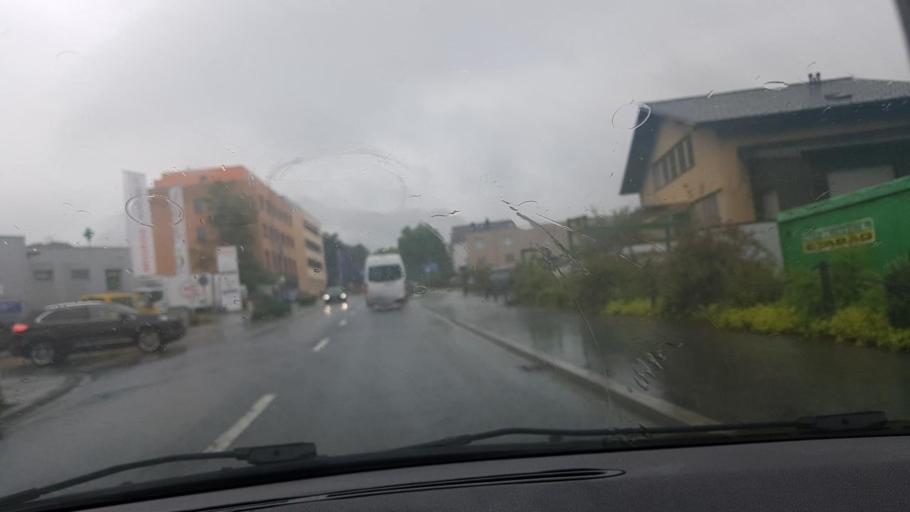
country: LI
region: Balzers
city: Balzers
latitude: 47.0759
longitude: 9.5120
